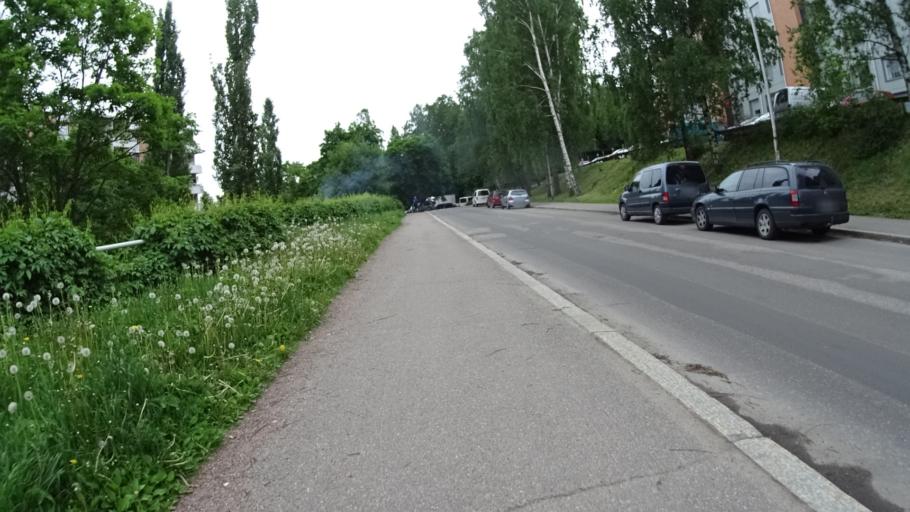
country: FI
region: Uusimaa
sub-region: Helsinki
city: Kilo
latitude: 60.2801
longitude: 24.8427
